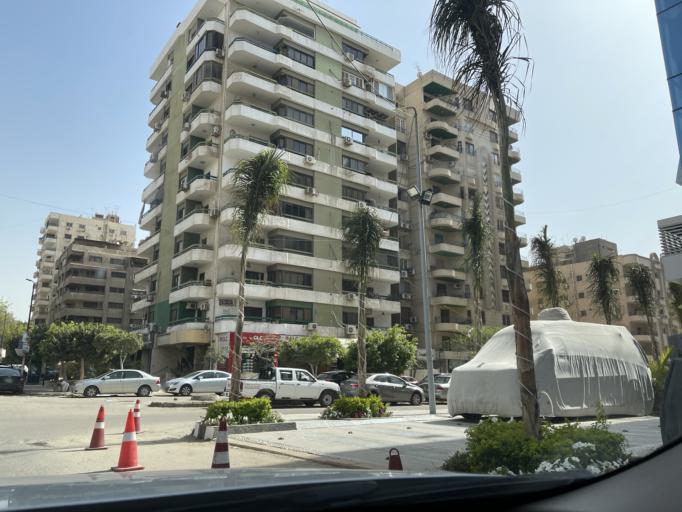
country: EG
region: Muhafazat al Qahirah
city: Cairo
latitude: 30.0606
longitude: 31.3535
